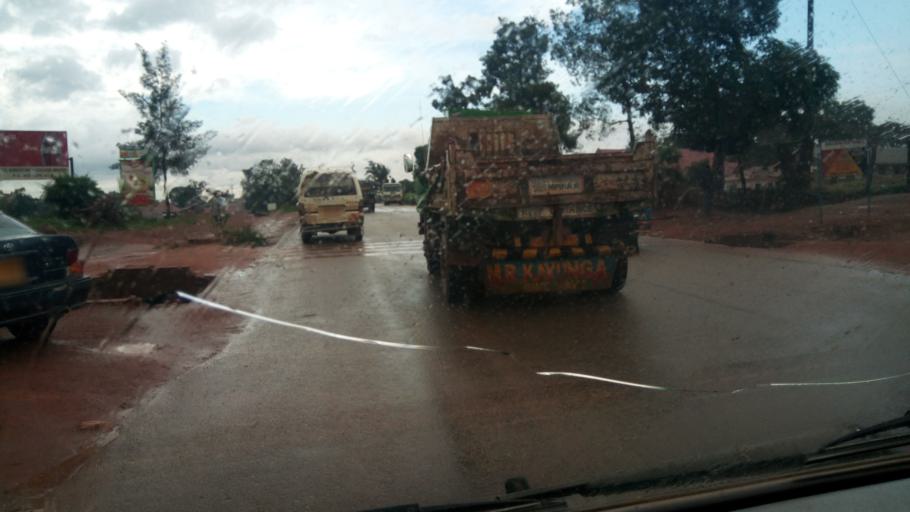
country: UG
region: Central Region
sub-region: Wakiso District
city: Wakiso
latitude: 0.3964
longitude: 32.4937
